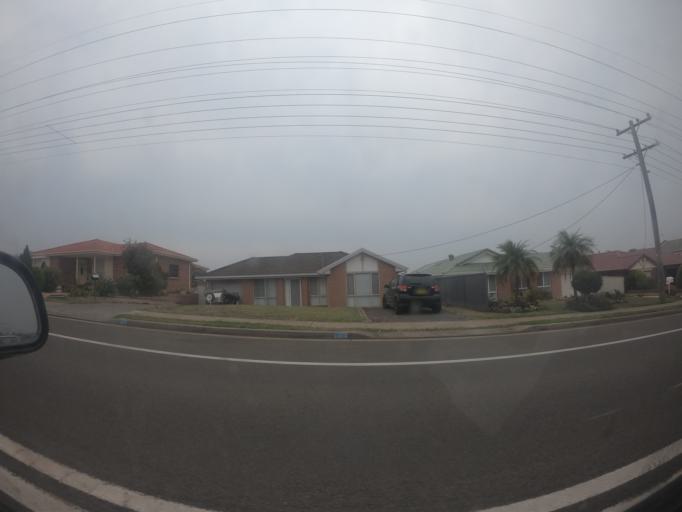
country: AU
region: New South Wales
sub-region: Shellharbour
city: Croom
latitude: -34.5748
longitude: 150.8368
